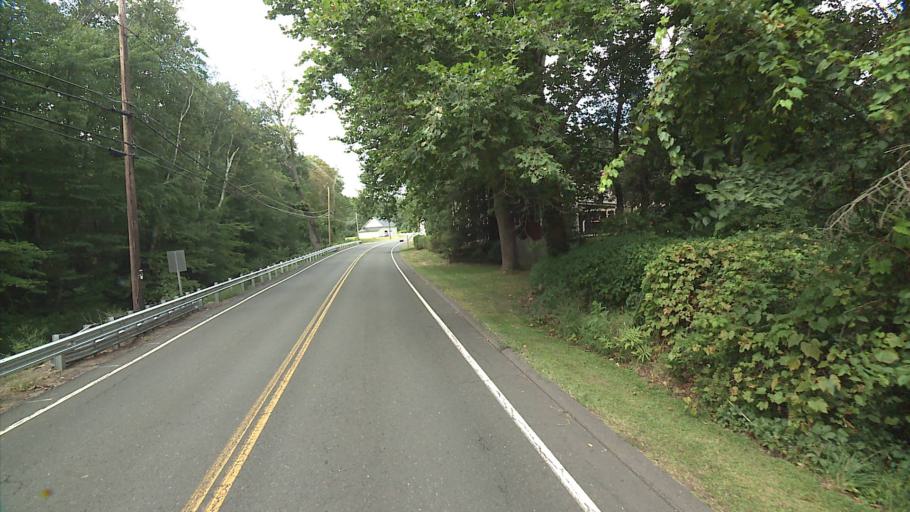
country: US
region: Connecticut
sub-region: Hartford County
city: North Granby
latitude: 42.0016
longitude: -72.8366
